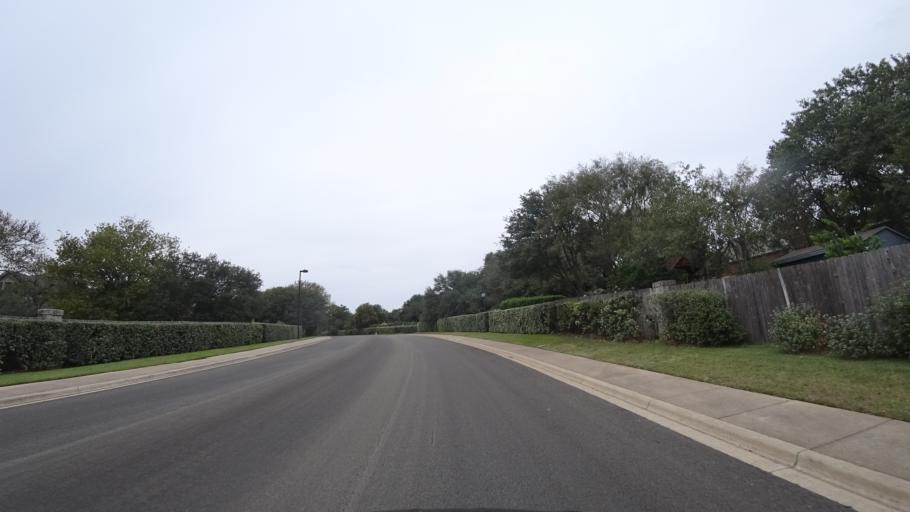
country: US
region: Texas
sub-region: Travis County
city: Shady Hollow
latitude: 30.1839
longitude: -97.8924
